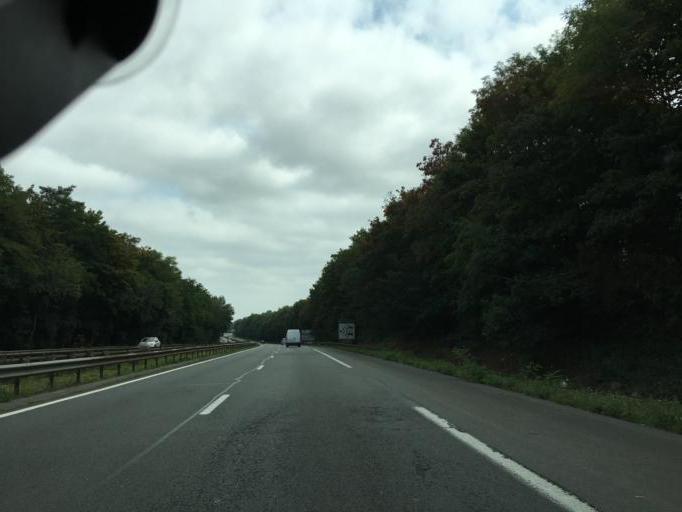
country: FR
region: Nord-Pas-de-Calais
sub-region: Departement du Pas-de-Calais
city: Courcelles-les-Lens
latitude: 50.4251
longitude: 3.0083
